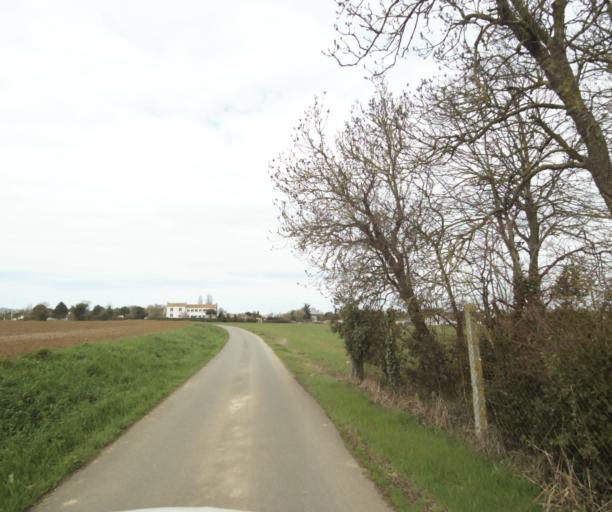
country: FR
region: Poitou-Charentes
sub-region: Departement de la Charente-Maritime
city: Nieul-sur-Mer
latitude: 46.1883
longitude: -1.1786
